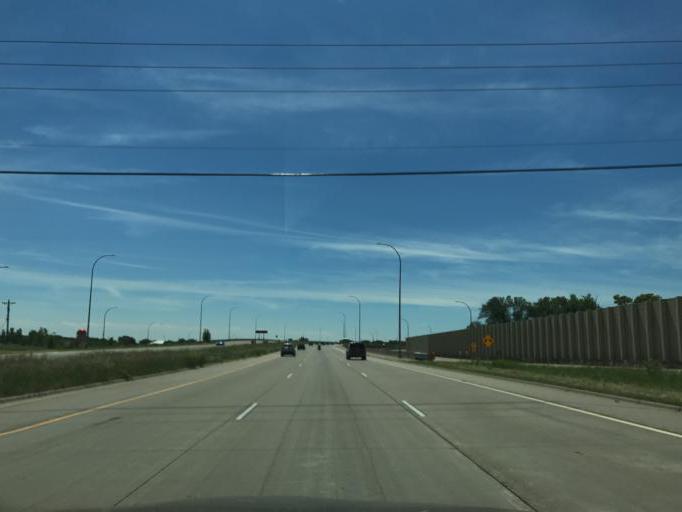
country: US
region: Minnesota
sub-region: Hennepin County
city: Osseo
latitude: 45.1132
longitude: -93.3914
